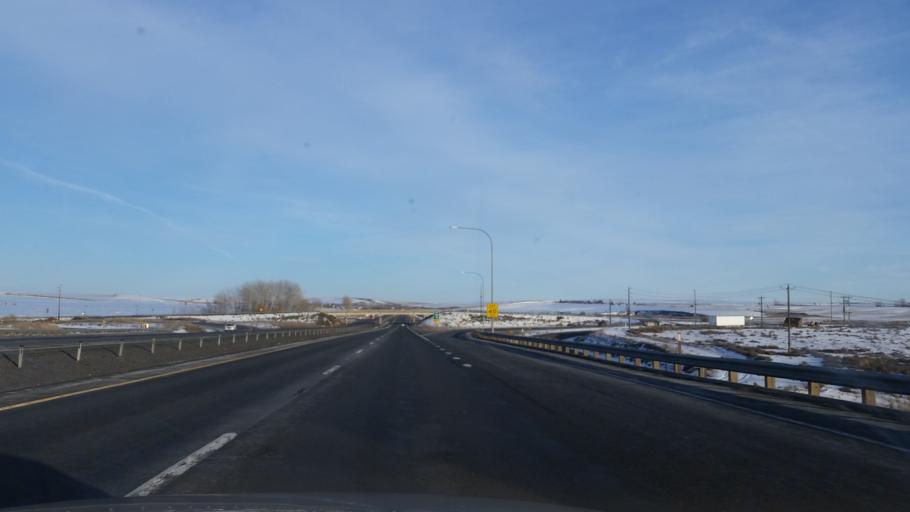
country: US
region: Washington
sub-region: Grant County
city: Warden
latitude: 47.0858
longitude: -119.0500
